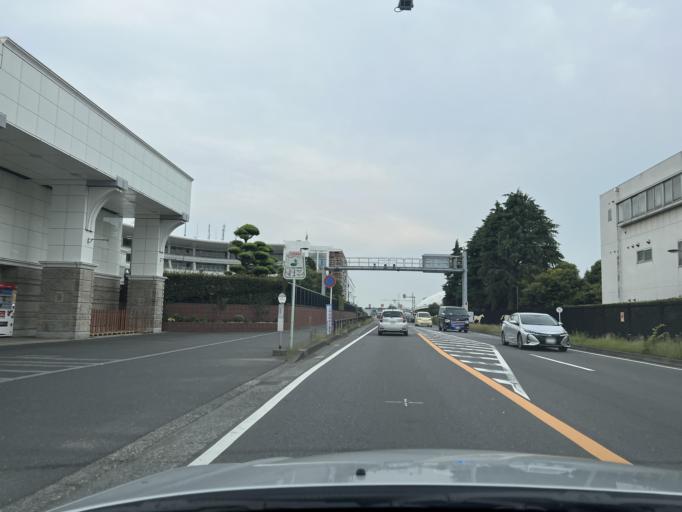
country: JP
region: Chiba
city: Funabashi
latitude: 35.7267
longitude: 139.9593
